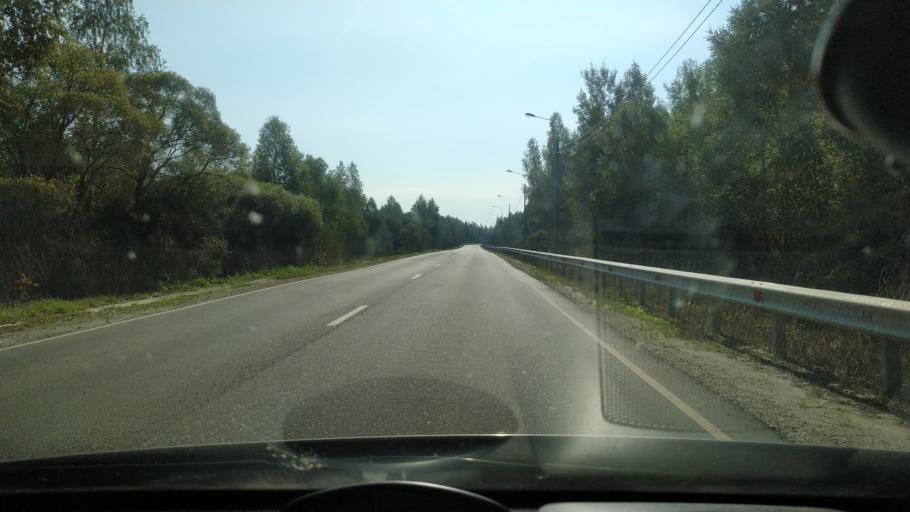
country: RU
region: Moskovskaya
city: Dmitrovskiy Pogost
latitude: 55.2309
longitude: 39.9168
